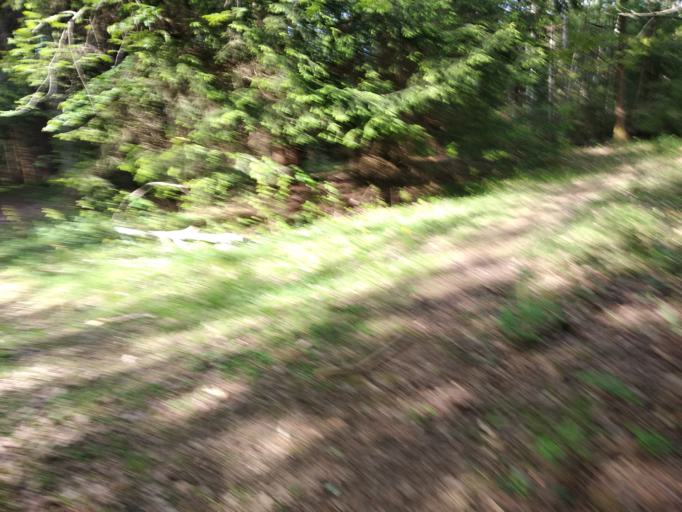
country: DE
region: Bavaria
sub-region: Upper Bavaria
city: Vaterstetten
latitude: 48.1158
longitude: 11.7603
